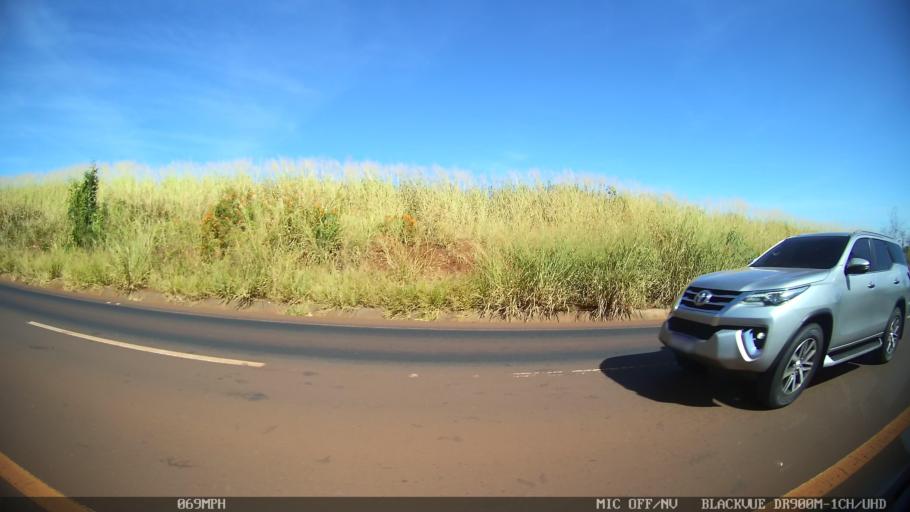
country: BR
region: Sao Paulo
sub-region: Sao Joaquim Da Barra
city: Sao Joaquim da Barra
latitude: -20.5495
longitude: -47.7521
